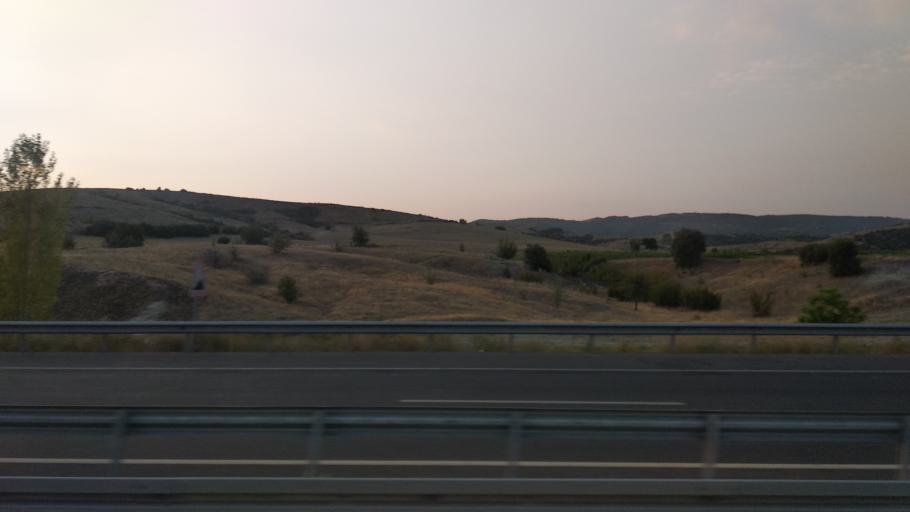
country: TR
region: Manisa
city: Selendi
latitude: 38.6244
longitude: 28.9288
